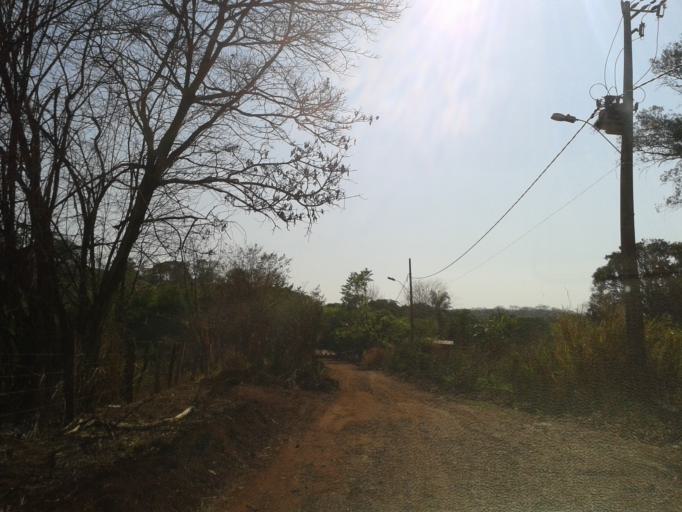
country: BR
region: Minas Gerais
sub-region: Ituiutaba
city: Ituiutaba
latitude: -18.9432
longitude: -49.4528
